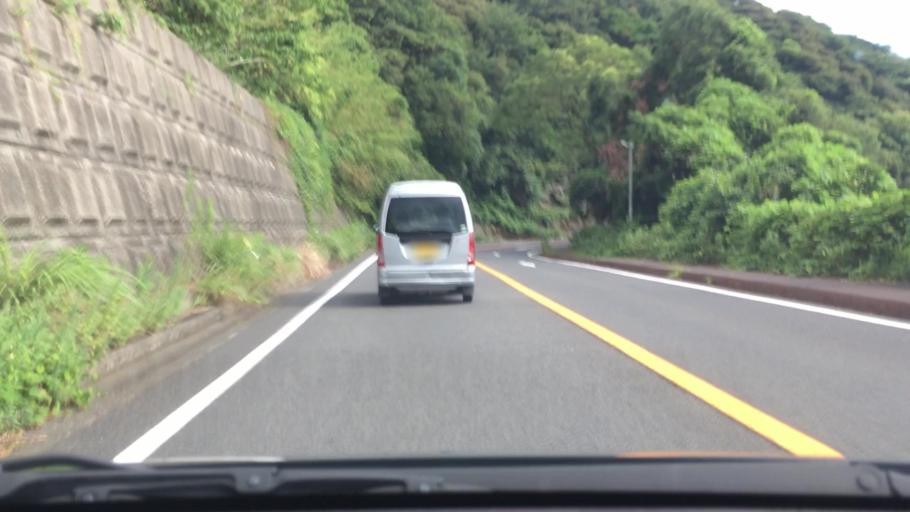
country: JP
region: Nagasaki
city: Togitsu
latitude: 32.8409
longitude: 129.7060
